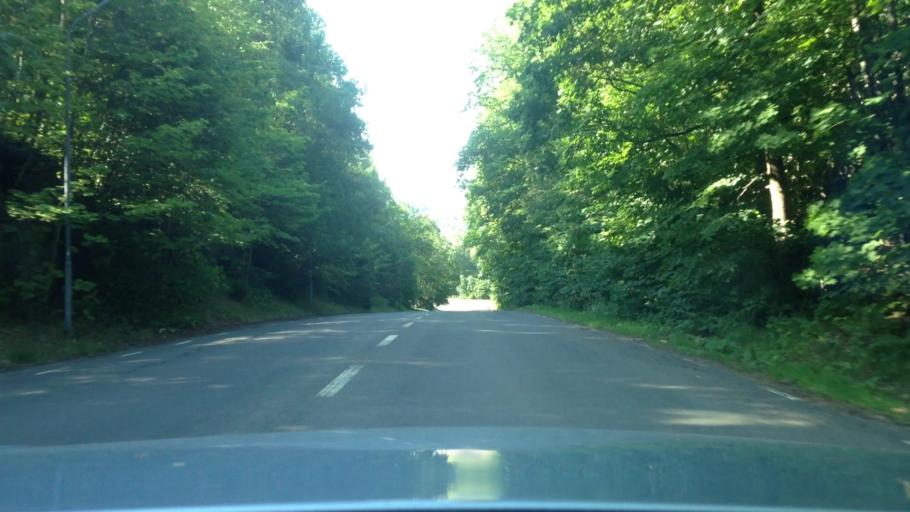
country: SE
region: Vaestra Goetaland
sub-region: Skovde Kommun
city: Skoevde
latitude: 58.4001
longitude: 13.8190
